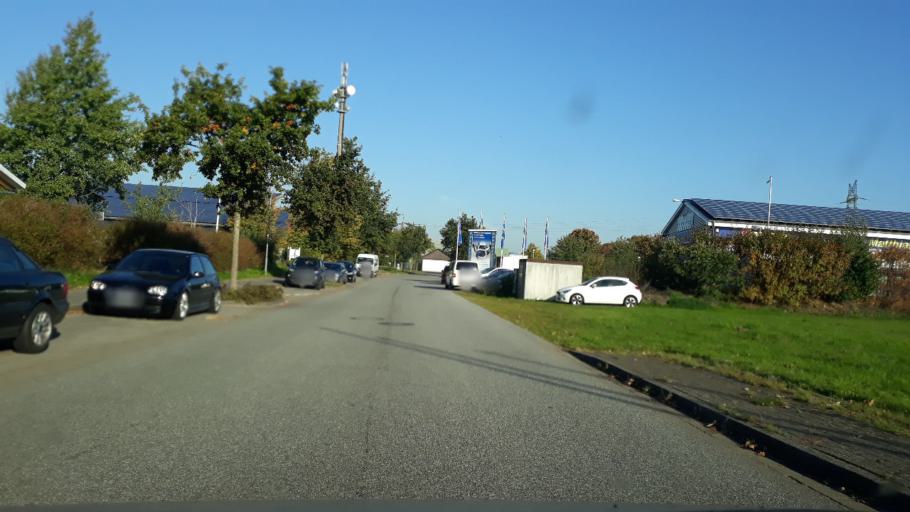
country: DE
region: Schleswig-Holstein
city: Kropp
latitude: 54.4146
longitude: 9.5281
